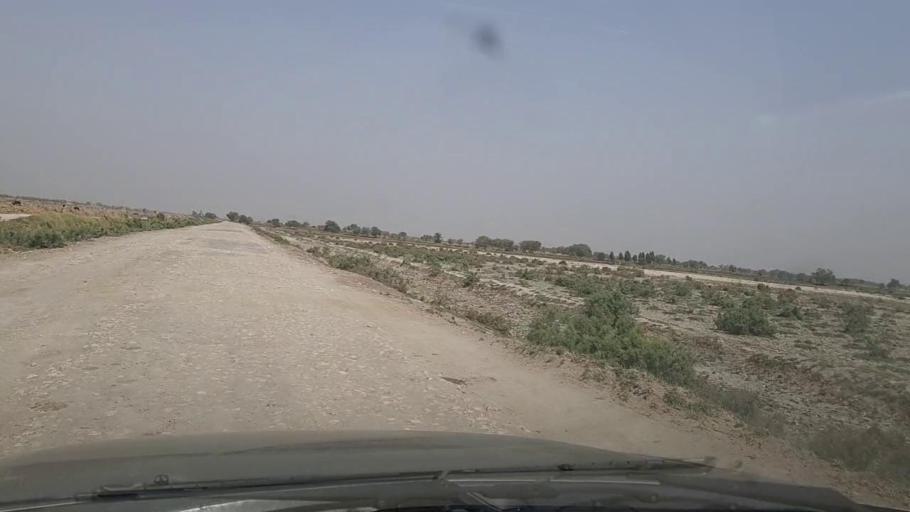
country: PK
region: Sindh
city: Thul
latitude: 28.4058
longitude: 68.7021
